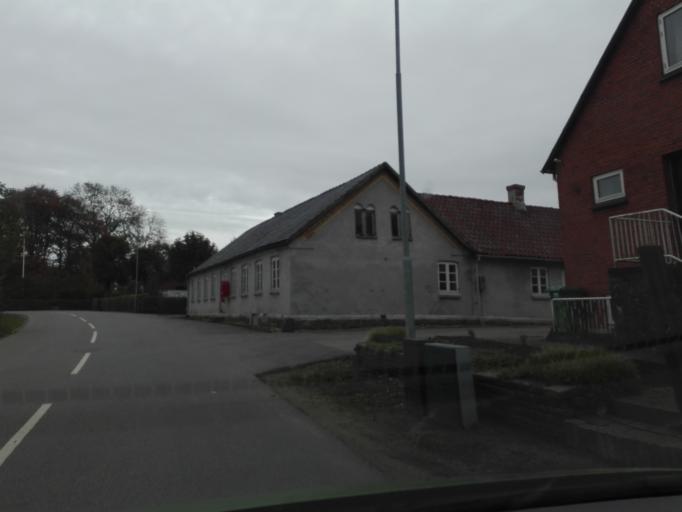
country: DK
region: Central Jutland
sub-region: Arhus Kommune
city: Tranbjerg
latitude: 56.0637
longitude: 10.1073
